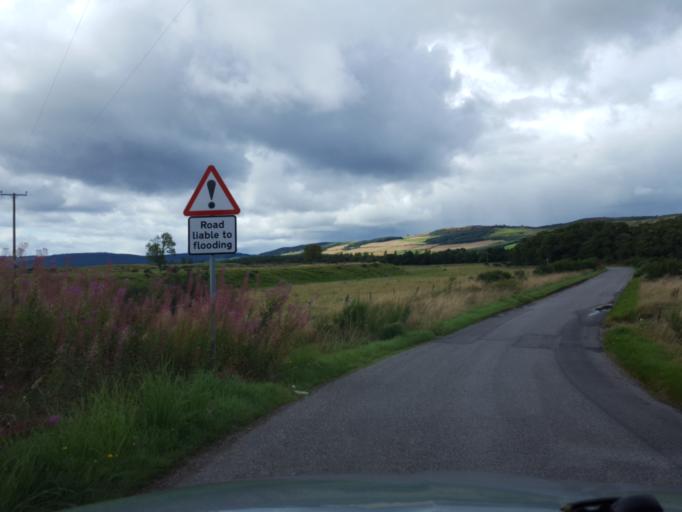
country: GB
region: Scotland
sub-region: Aberdeenshire
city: Torphins
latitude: 57.0165
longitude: -2.5862
